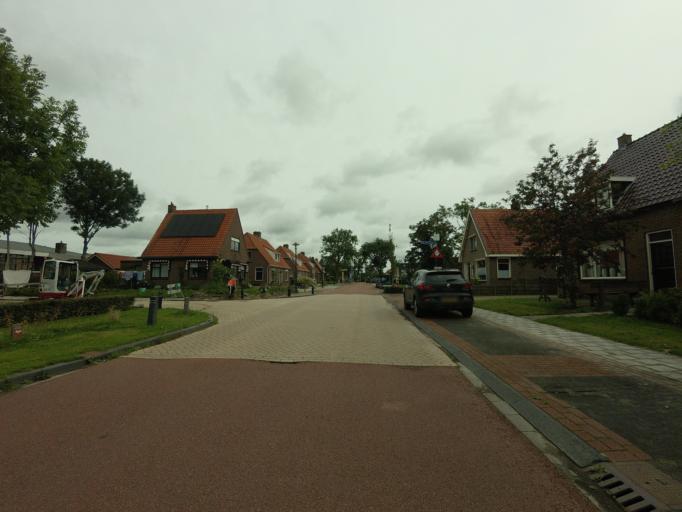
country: NL
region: Overijssel
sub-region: Gemeente Steenwijkerland
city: Oldemarkt
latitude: 52.8078
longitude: 5.9165
